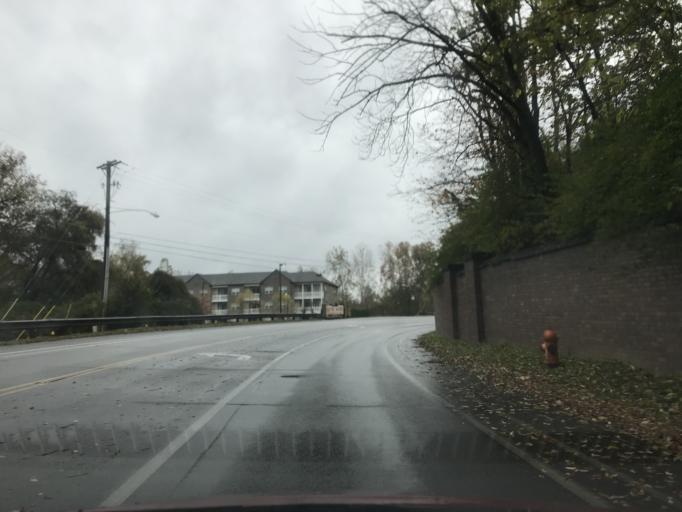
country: US
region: Indiana
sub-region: Clark County
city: Jeffersonville
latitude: 38.2477
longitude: -85.7083
